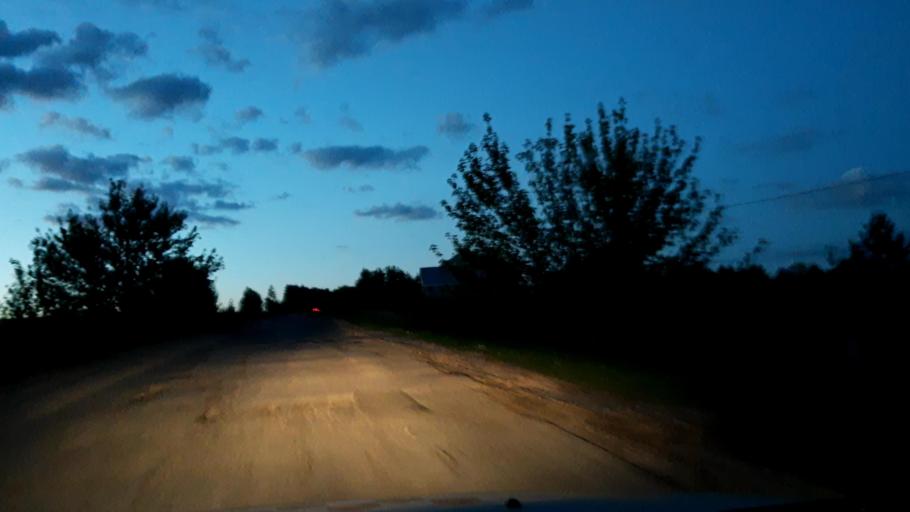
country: RU
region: Nizjnij Novgorod
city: Pamyat' Parizhskoy Kommuny
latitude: 56.0478
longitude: 44.4364
